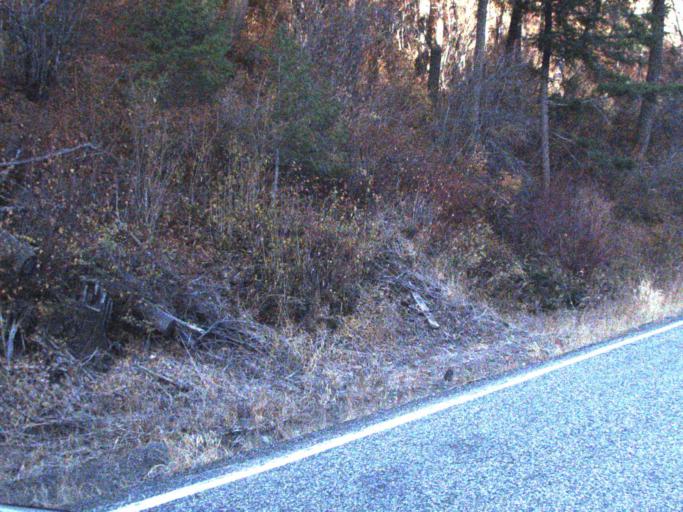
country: US
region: Washington
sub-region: Ferry County
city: Republic
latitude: 48.5248
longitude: -118.7347
